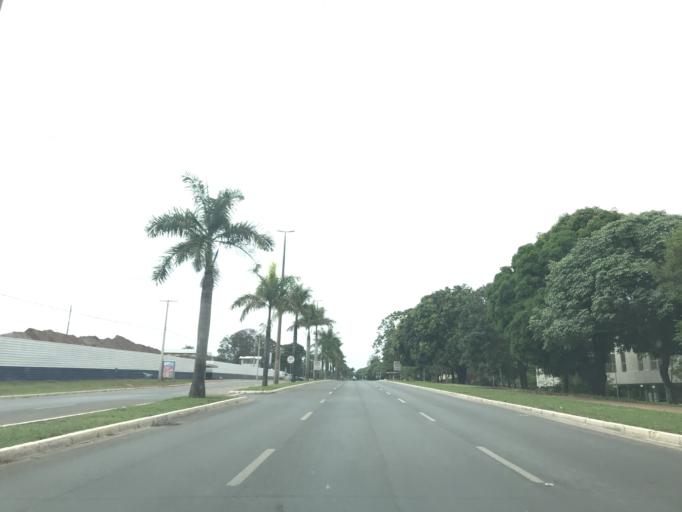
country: BR
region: Federal District
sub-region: Brasilia
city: Brasilia
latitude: -15.7474
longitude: -47.8820
